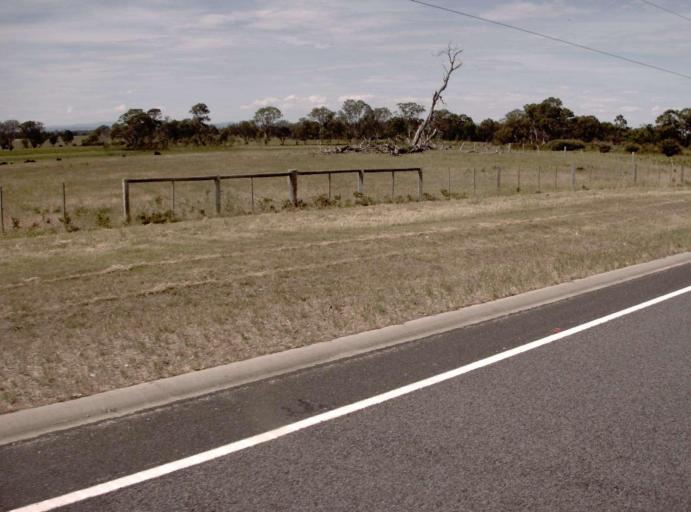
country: AU
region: Victoria
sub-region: East Gippsland
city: Bairnsdale
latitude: -37.9053
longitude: 147.3348
